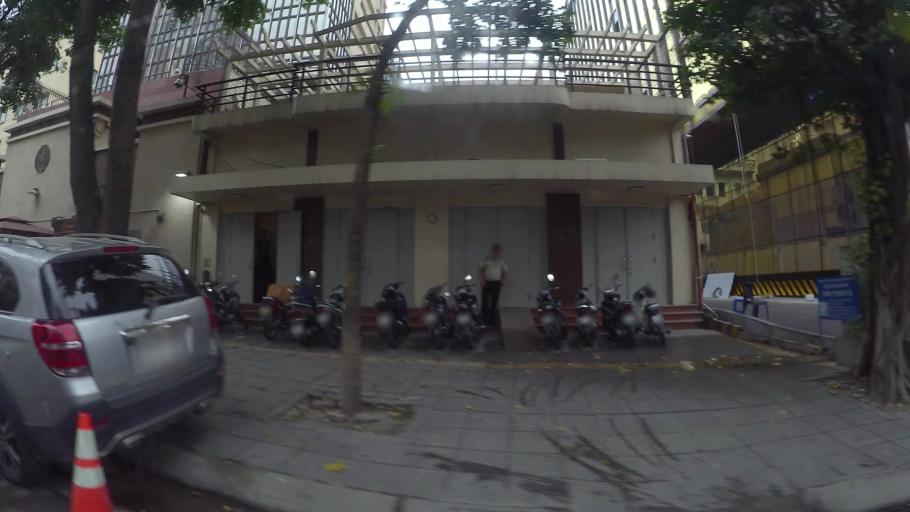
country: VN
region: Ha Noi
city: Dong Da
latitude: 21.0216
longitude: 105.8187
